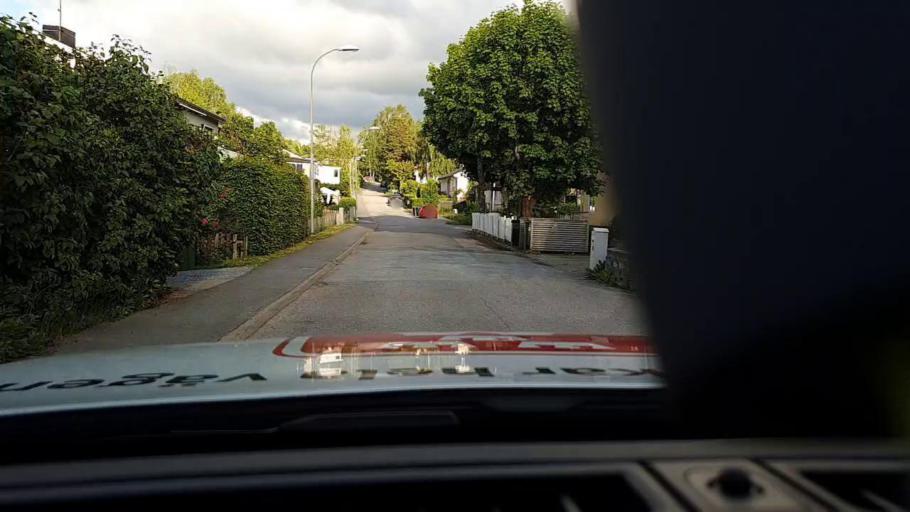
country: SE
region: Stockholm
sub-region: Huddinge Kommun
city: Huddinge
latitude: 59.2488
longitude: 17.9630
